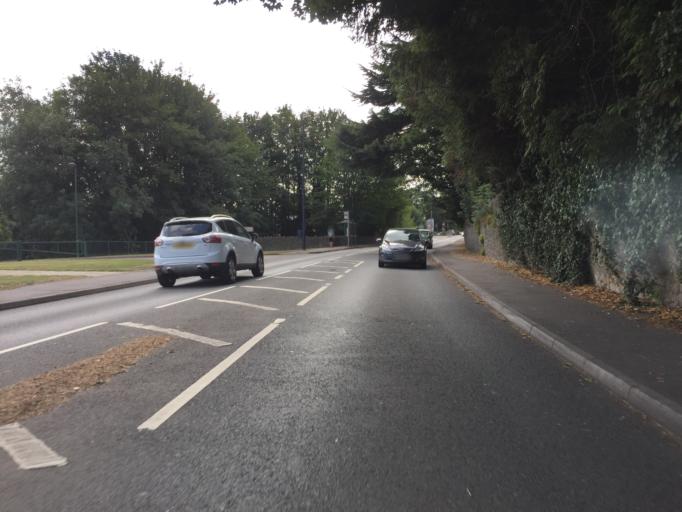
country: GB
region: England
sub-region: Kent
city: Maidstone
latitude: 51.2797
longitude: 0.5066
